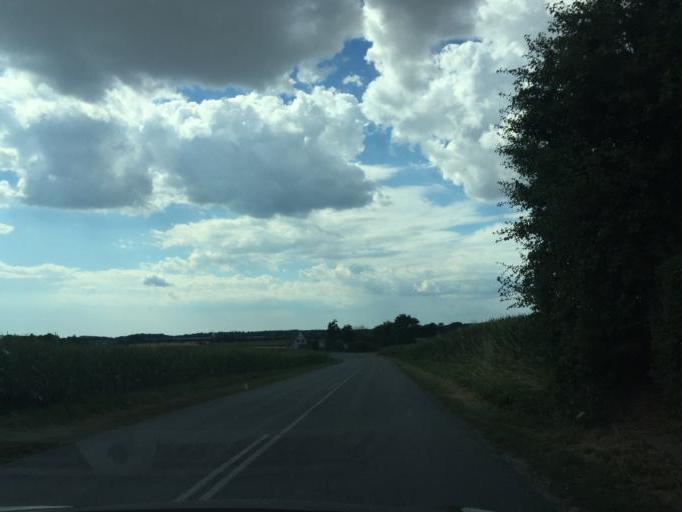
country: DK
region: South Denmark
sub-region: Assens Kommune
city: Harby
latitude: 55.2164
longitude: 10.0492
